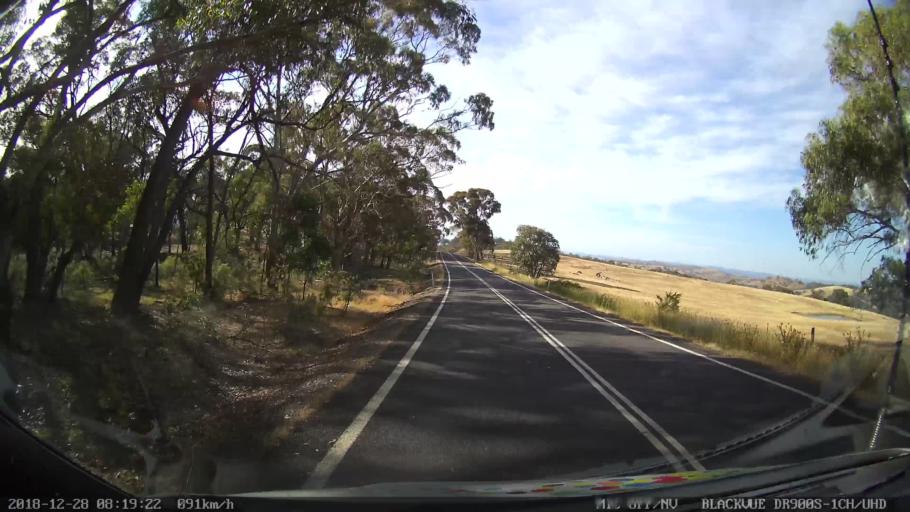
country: AU
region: New South Wales
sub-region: Blayney
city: Blayney
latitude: -33.8582
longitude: 149.3507
